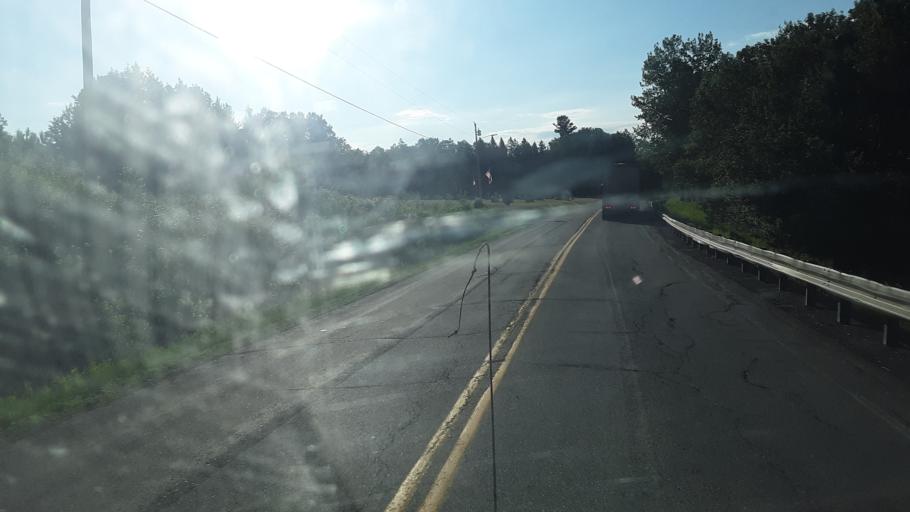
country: US
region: Maine
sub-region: Penobscot County
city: Patten
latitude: 46.1344
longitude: -68.1834
